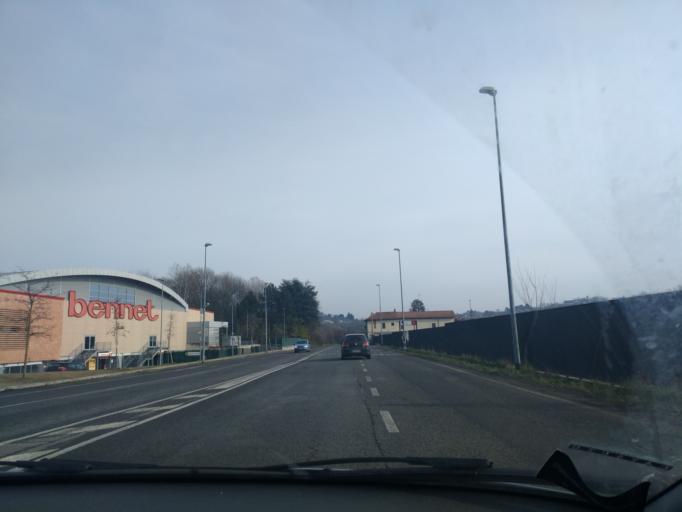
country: IT
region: Lombardy
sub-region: Provincia di Como
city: Anzano del Parco
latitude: 45.7622
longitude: 9.2046
